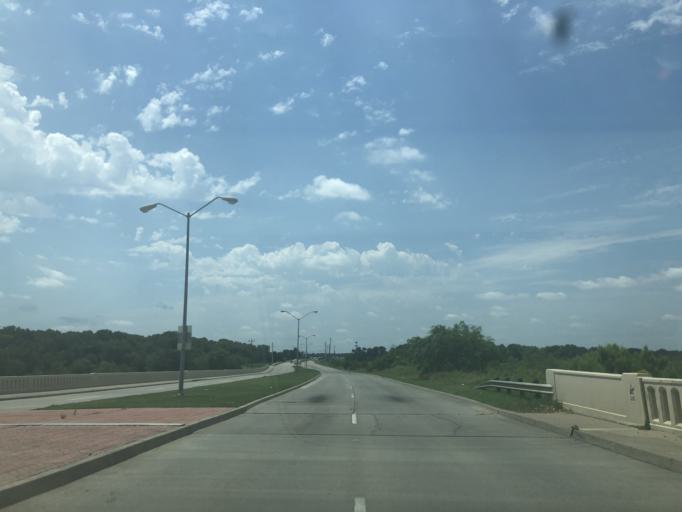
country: US
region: Texas
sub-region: Dallas County
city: Irving
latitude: 32.7787
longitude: -96.9603
